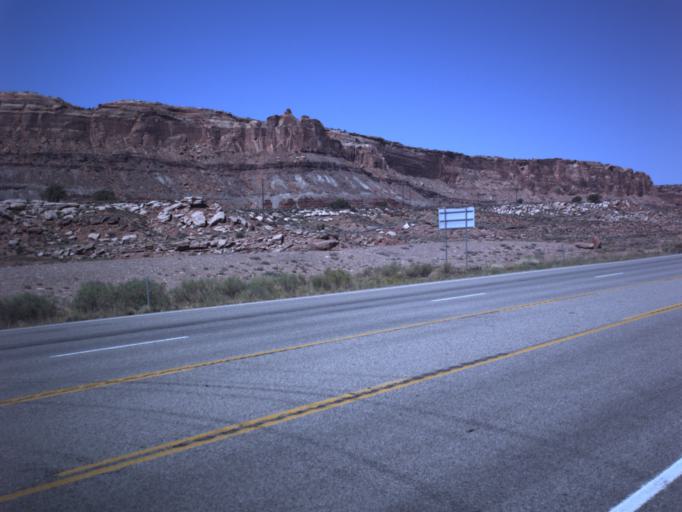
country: US
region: Utah
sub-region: Grand County
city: Moab
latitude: 38.6739
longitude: -109.6873
